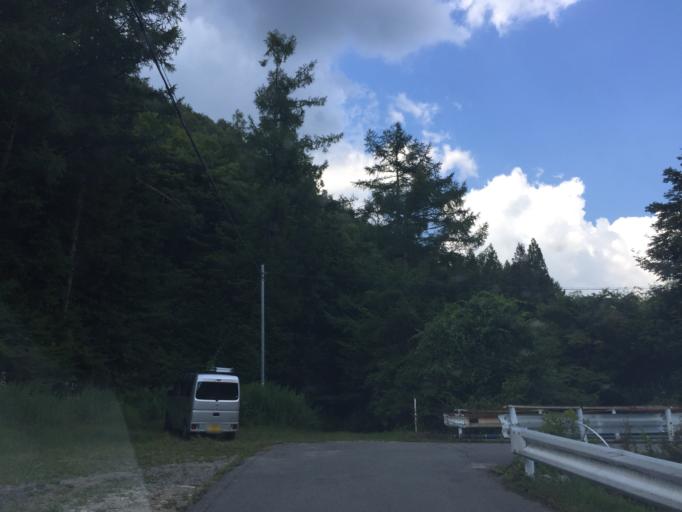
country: JP
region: Nagano
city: Iida
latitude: 35.3967
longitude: 137.6853
